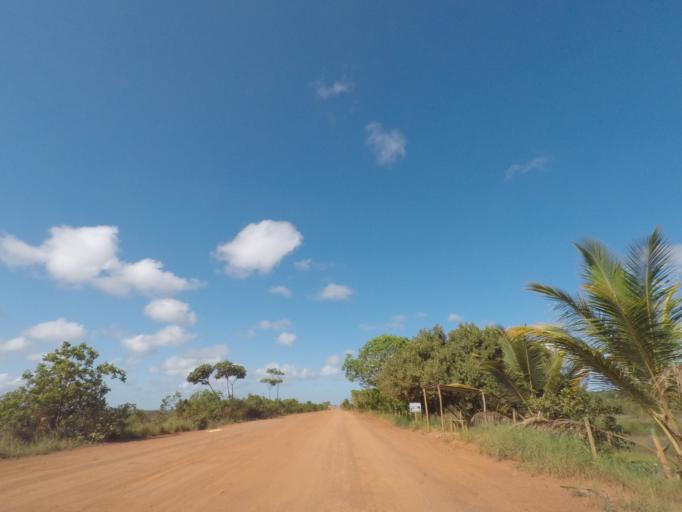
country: BR
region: Bahia
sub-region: Marau
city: Marau
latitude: -14.1823
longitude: -39.0240
